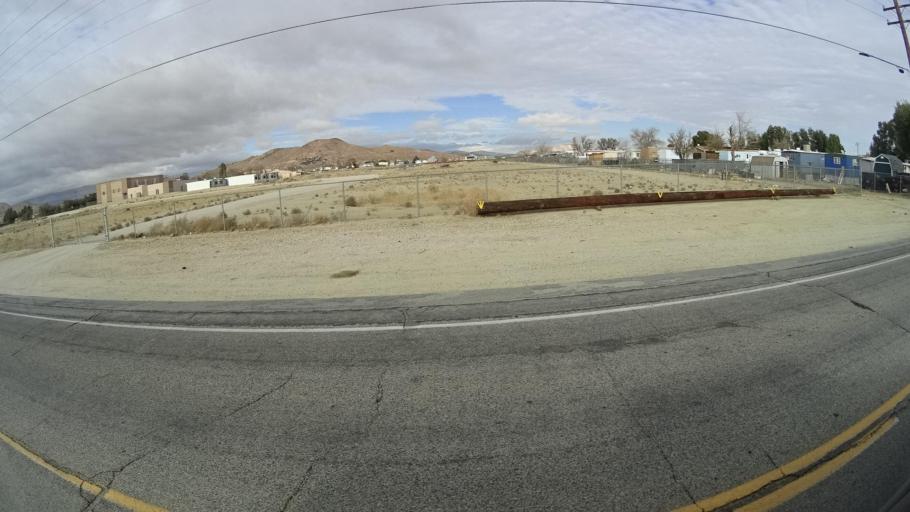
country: US
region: California
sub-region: Kern County
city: Rosamond
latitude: 34.8637
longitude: -118.2267
